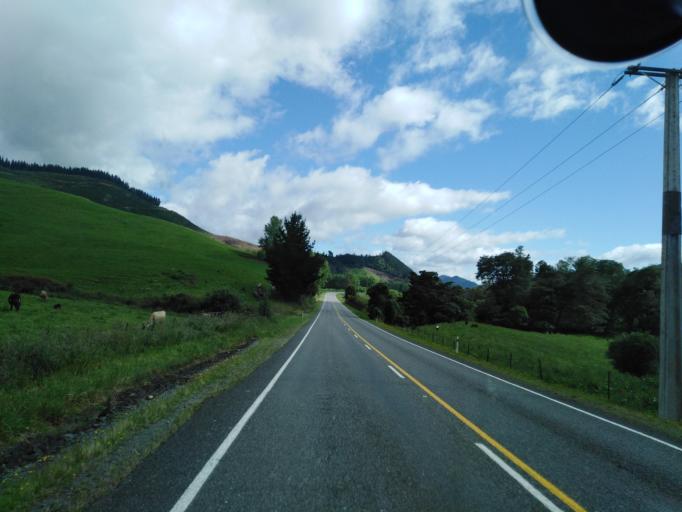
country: NZ
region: Nelson
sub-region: Nelson City
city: Nelson
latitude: -41.2725
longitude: 173.5728
